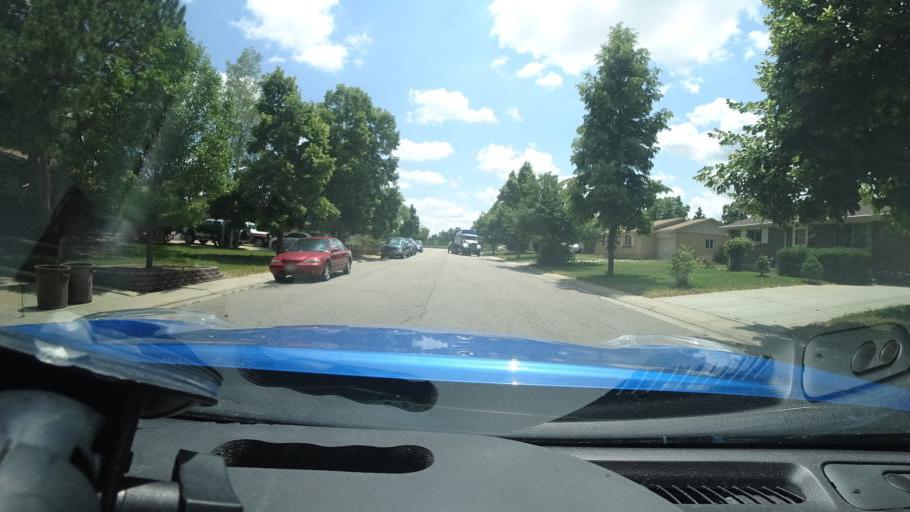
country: US
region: Colorado
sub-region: Adams County
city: Aurora
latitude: 39.7082
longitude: -104.8431
